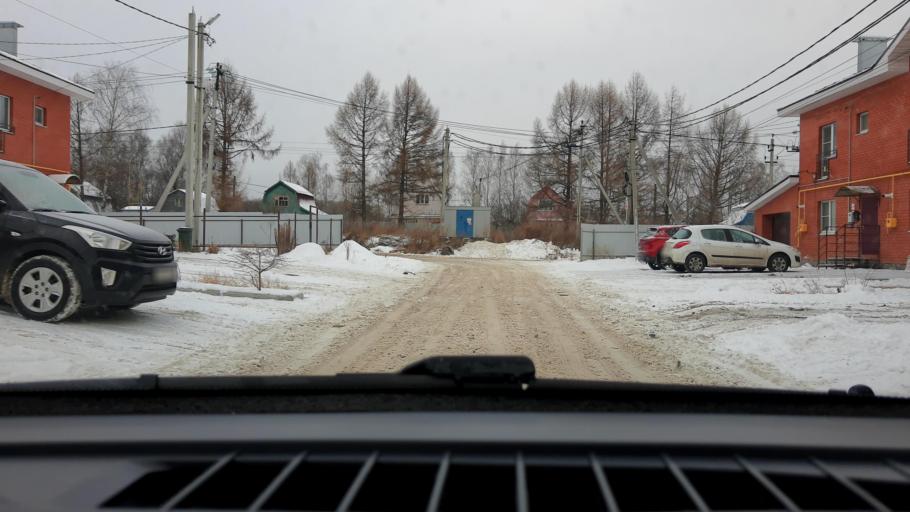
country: RU
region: Nizjnij Novgorod
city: Afonino
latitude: 56.2179
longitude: 44.0860
